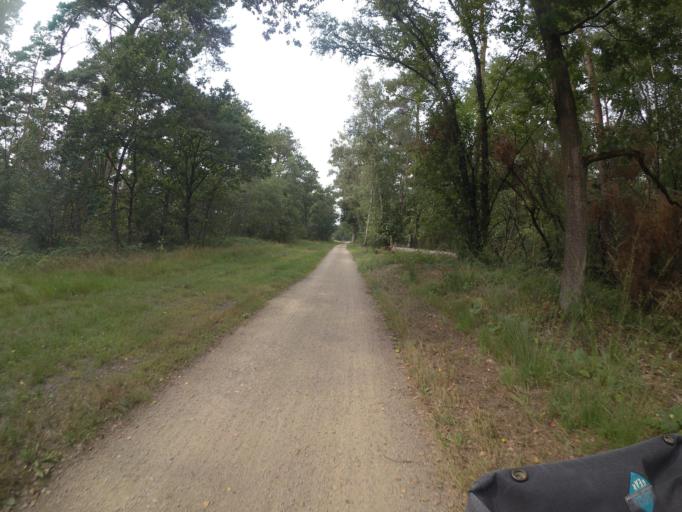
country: DE
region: North Rhine-Westphalia
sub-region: Regierungsbezirk Dusseldorf
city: Goch
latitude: 51.6208
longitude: 6.0714
